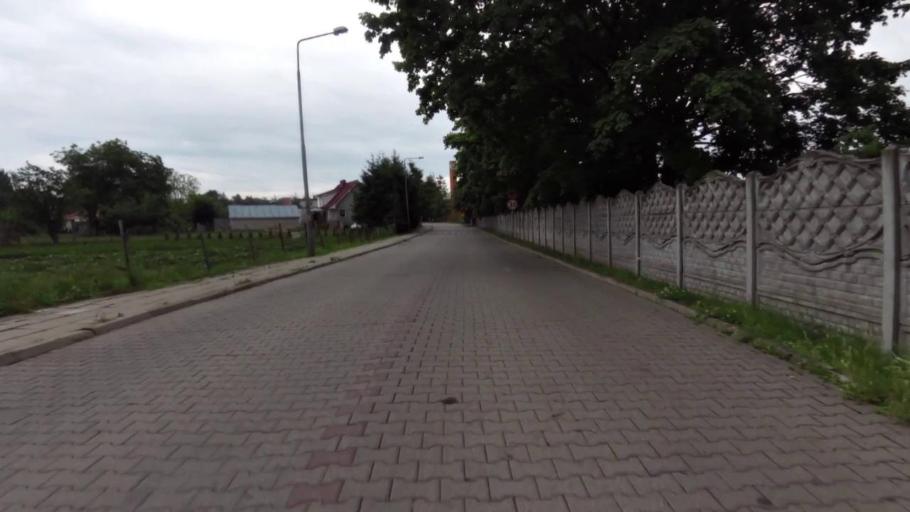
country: PL
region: West Pomeranian Voivodeship
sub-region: Powiat mysliborski
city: Mysliborz
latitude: 52.9282
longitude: 14.8598
